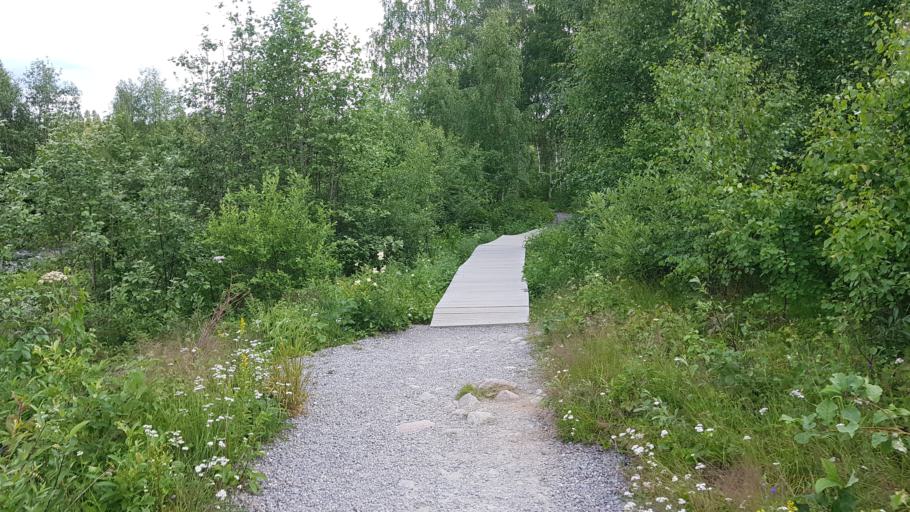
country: SE
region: Norrbotten
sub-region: Alvsbyns Kommun
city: AElvsbyn
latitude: 65.8549
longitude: 20.4154
